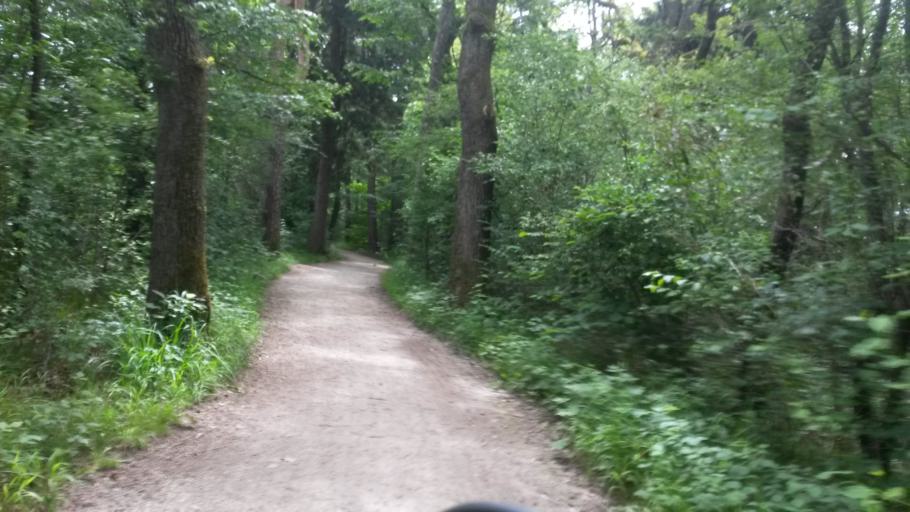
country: DE
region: Bavaria
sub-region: Upper Bavaria
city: Ubersee
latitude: 47.8575
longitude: 12.4821
